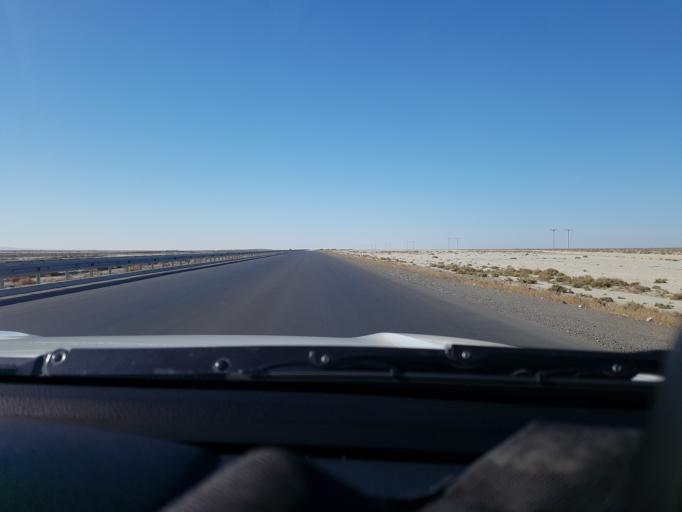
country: TM
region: Balkan
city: Gazanjyk
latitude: 39.2540
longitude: 55.1040
